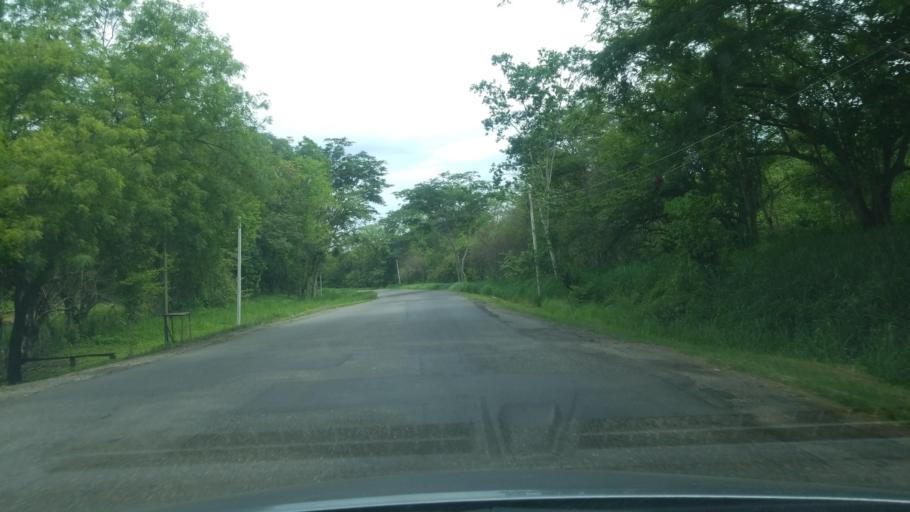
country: HN
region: Santa Barbara
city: Camalote
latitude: 15.3248
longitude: -88.3167
